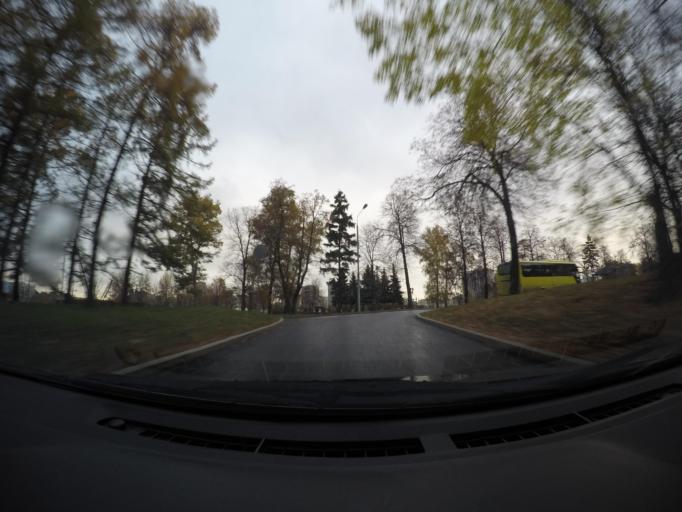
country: RU
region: Moskovskaya
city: Kastanayevo
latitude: 55.7307
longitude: 37.4927
